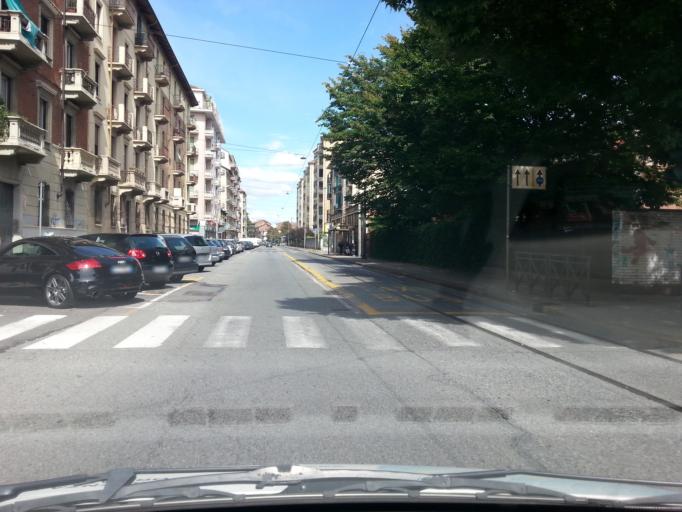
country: IT
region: Piedmont
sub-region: Provincia di Torino
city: Moncalieri
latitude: 45.0343
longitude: 7.6704
